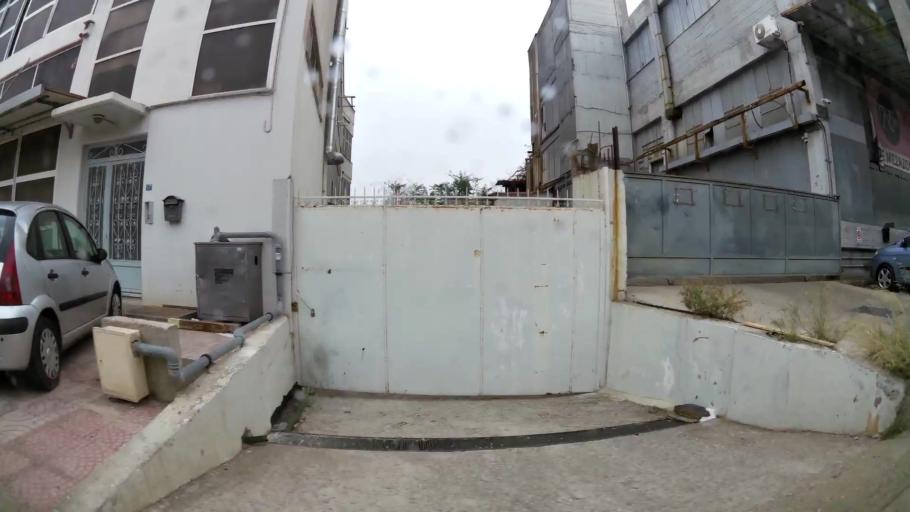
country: GR
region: Attica
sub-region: Nomarchia Athinas
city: Peristeri
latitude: 38.0075
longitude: 23.7118
